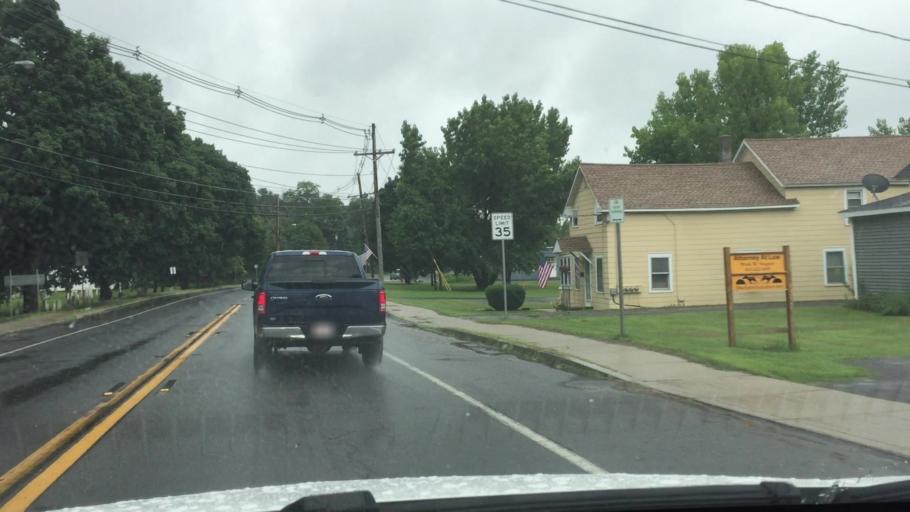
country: US
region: Massachusetts
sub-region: Berkshire County
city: Lanesborough
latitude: 42.5160
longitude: -73.2280
